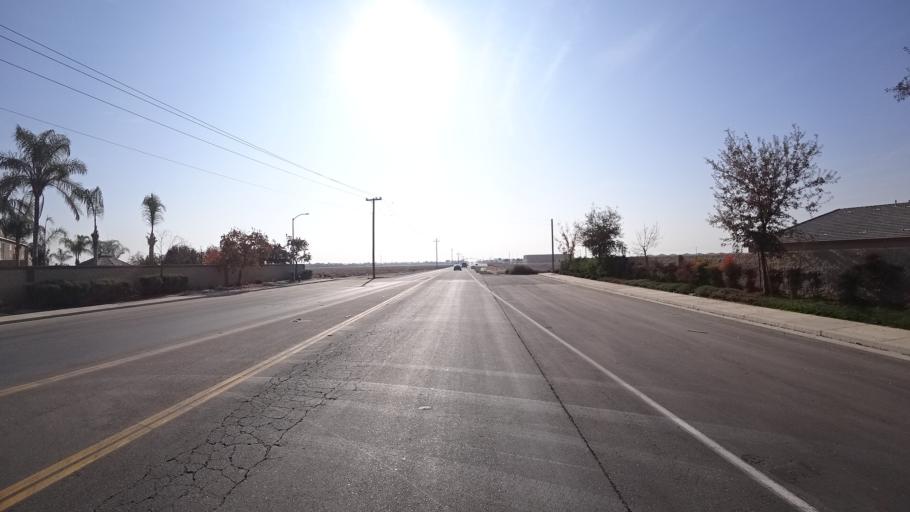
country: US
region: California
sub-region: Kern County
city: Greenacres
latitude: 35.3002
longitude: -119.1099
